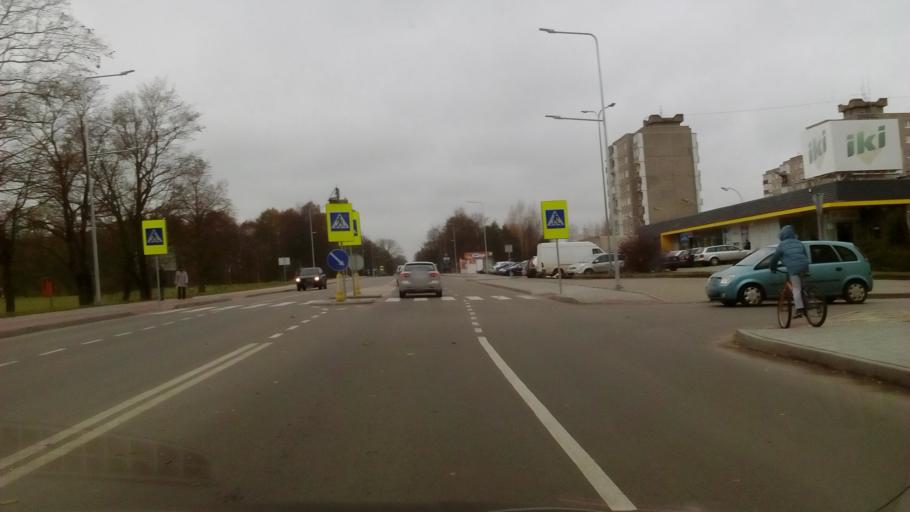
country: LT
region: Marijampoles apskritis
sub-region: Marijampole Municipality
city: Marijampole
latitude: 54.5627
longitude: 23.3336
